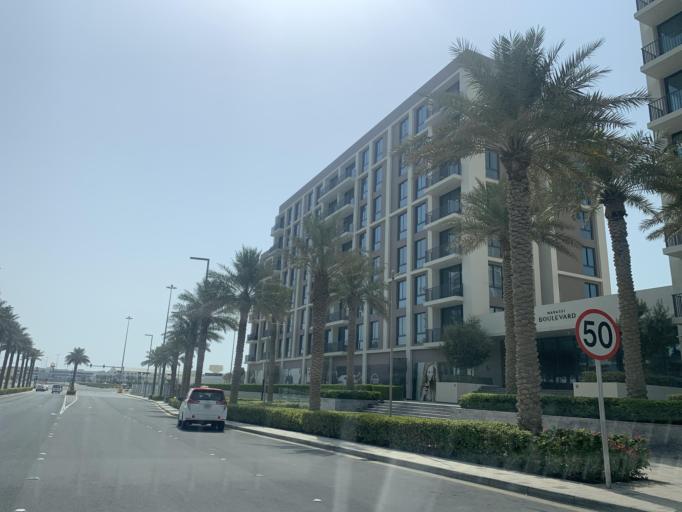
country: BH
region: Muharraq
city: Al Muharraq
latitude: 26.3062
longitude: 50.6425
